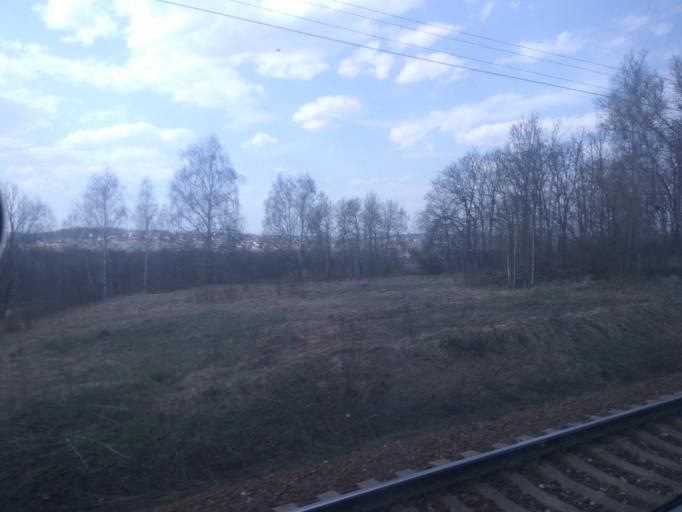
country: RU
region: Moskovskaya
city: Dedenevo
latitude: 56.2547
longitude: 37.5055
